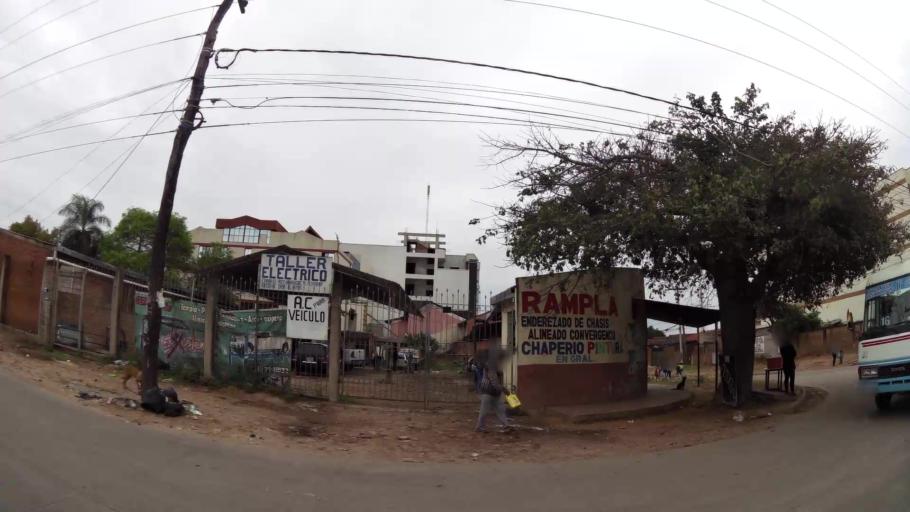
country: BO
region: Santa Cruz
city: Santa Cruz de la Sierra
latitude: -17.8229
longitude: -63.1807
